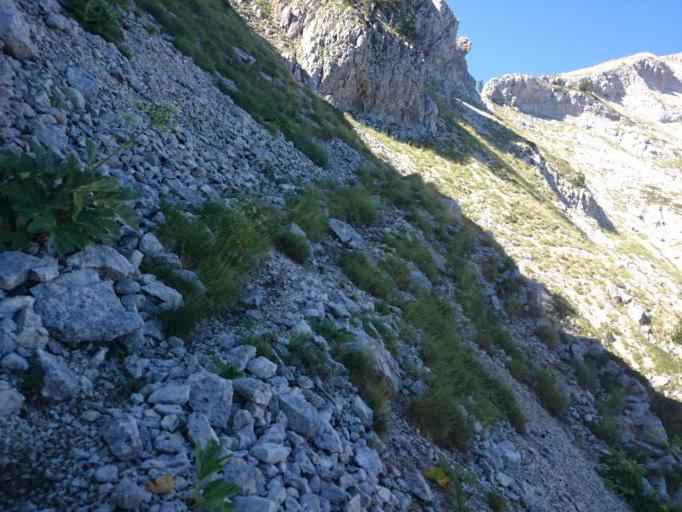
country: AL
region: Elbasan
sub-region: Rrethi i Gramshit
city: Kushove
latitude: 40.7125
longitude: 20.1508
